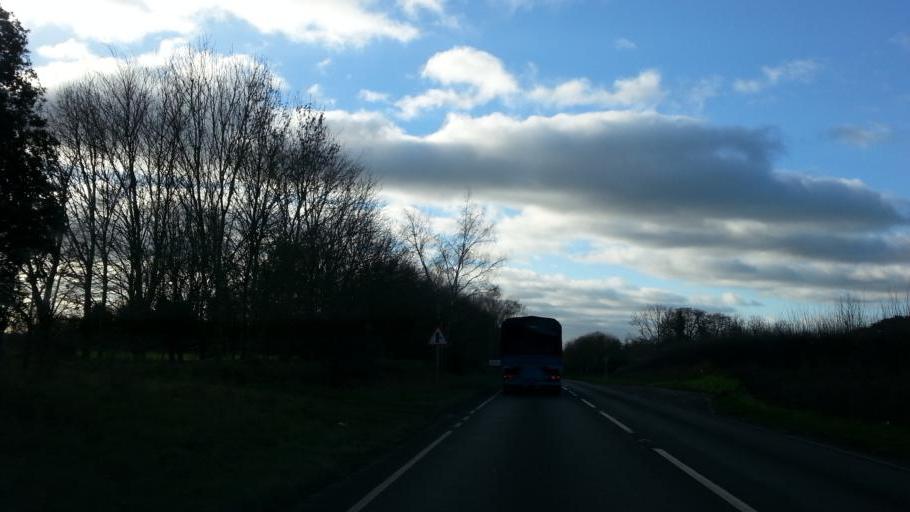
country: GB
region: England
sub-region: Norfolk
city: Harleston
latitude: 52.3656
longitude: 1.2209
